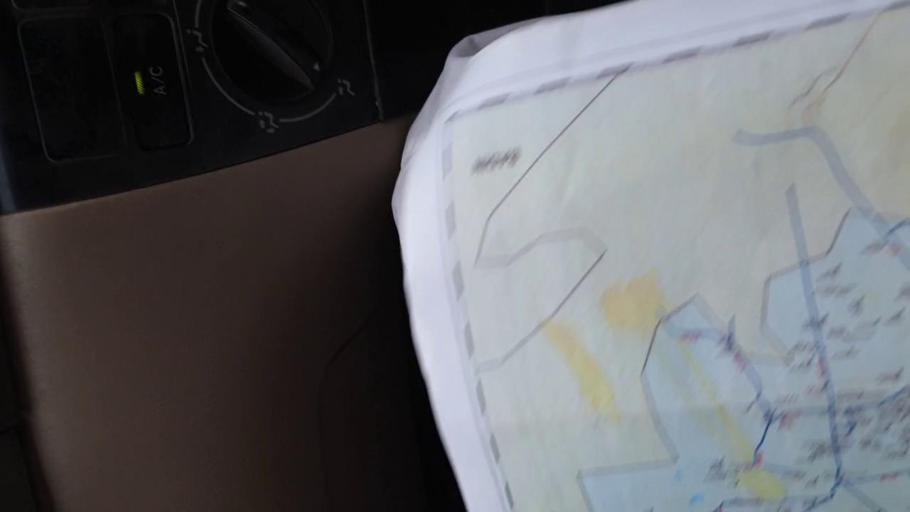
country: PK
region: Sindh
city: Tando Jam
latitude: 25.4325
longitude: 68.5525
